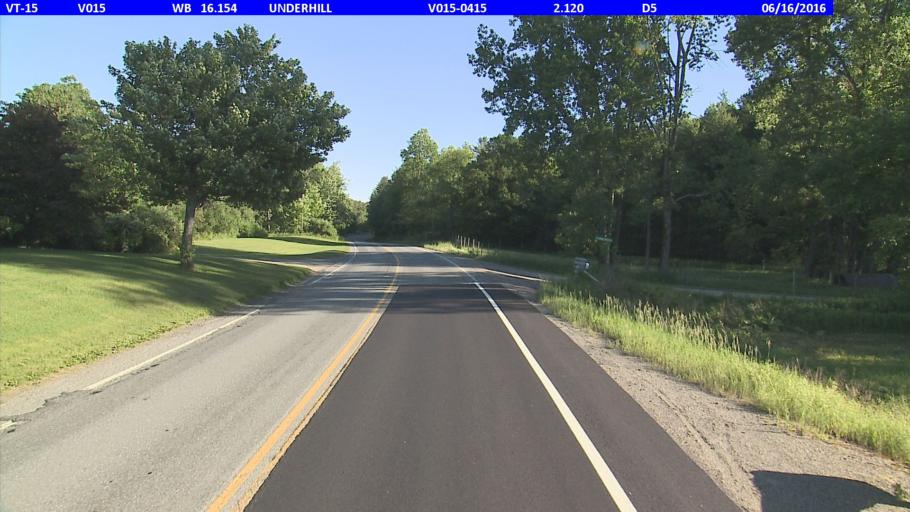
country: US
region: Vermont
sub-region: Chittenden County
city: Jericho
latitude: 44.5544
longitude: -72.9449
